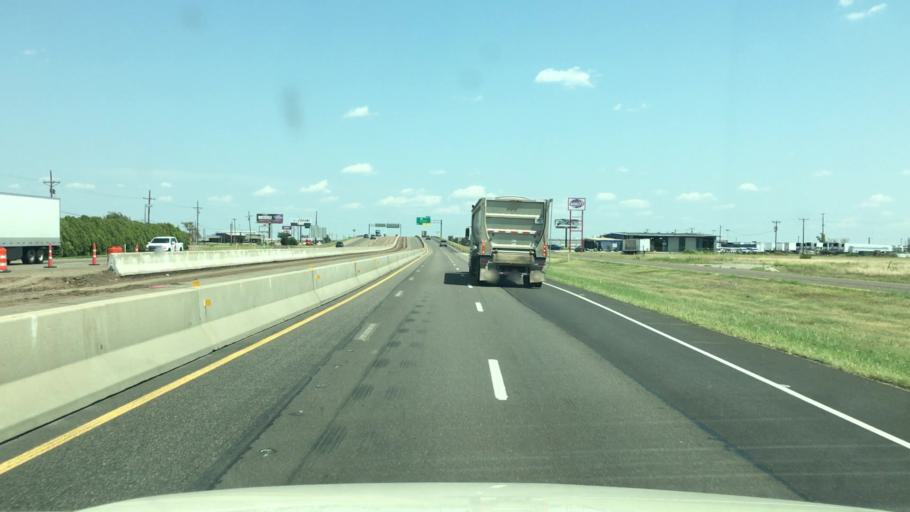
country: US
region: Texas
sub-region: Potter County
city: Amarillo
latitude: 35.1927
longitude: -101.7129
